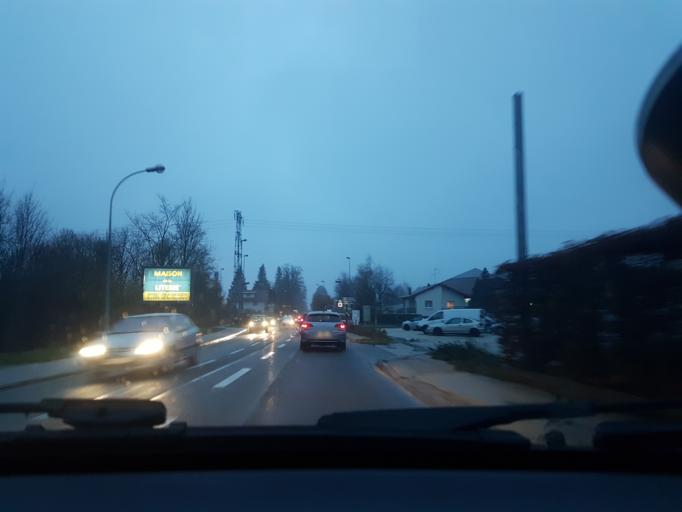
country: FR
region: Franche-Comte
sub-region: Departement du Doubs
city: Pontarlier
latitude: 46.8935
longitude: 6.3648
